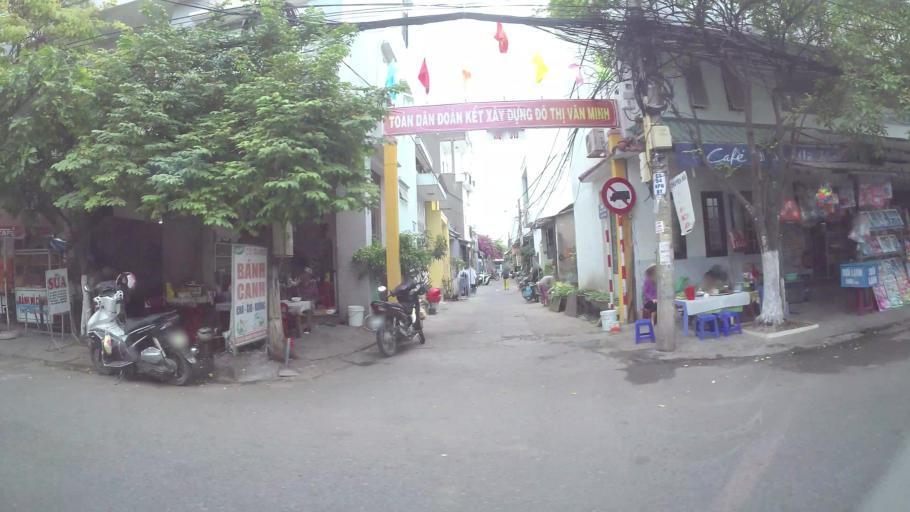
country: VN
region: Da Nang
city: Thanh Khe
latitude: 16.0530
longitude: 108.1844
